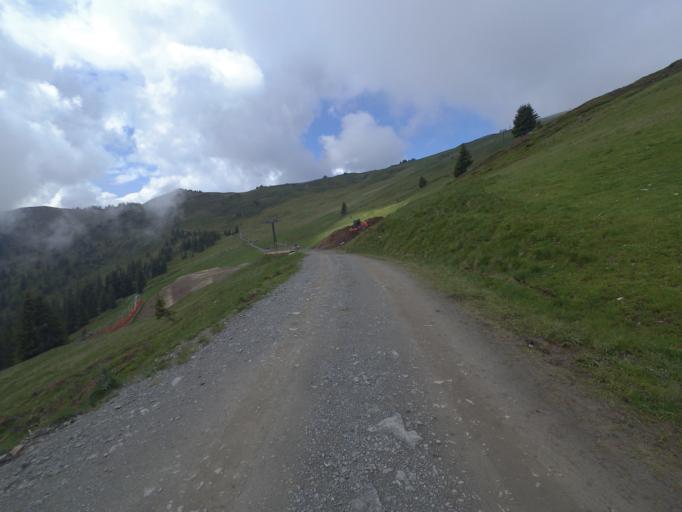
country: AT
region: Salzburg
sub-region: Politischer Bezirk Zell am See
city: Viehhofen
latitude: 47.4034
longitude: 12.7089
